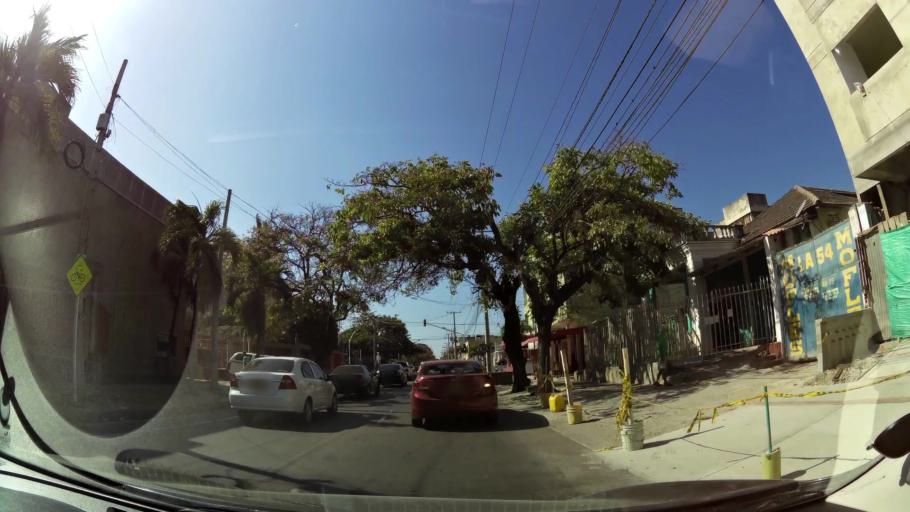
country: CO
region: Atlantico
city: Barranquilla
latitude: 10.9896
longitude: -74.7909
